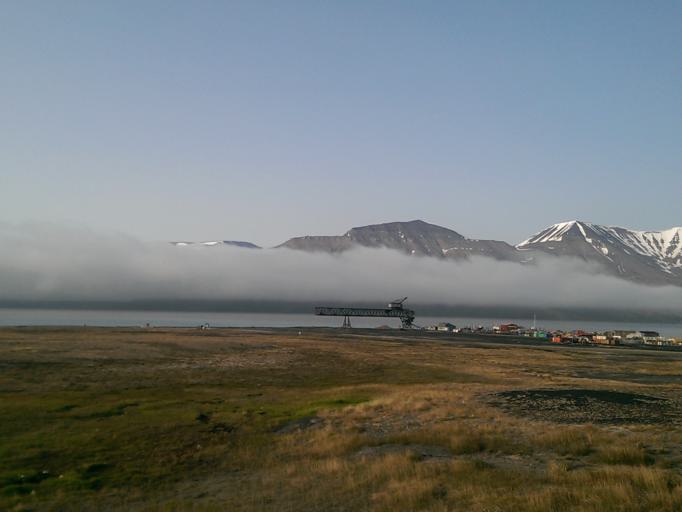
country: SJ
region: Svalbard
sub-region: Spitsbergen
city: Longyearbyen
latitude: 78.2438
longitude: 15.5229
